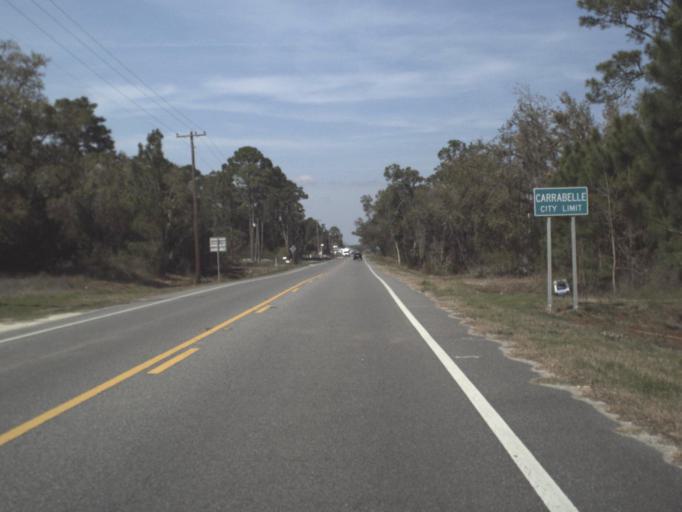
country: US
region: Florida
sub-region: Franklin County
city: Carrabelle
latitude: 29.8356
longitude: -84.6829
